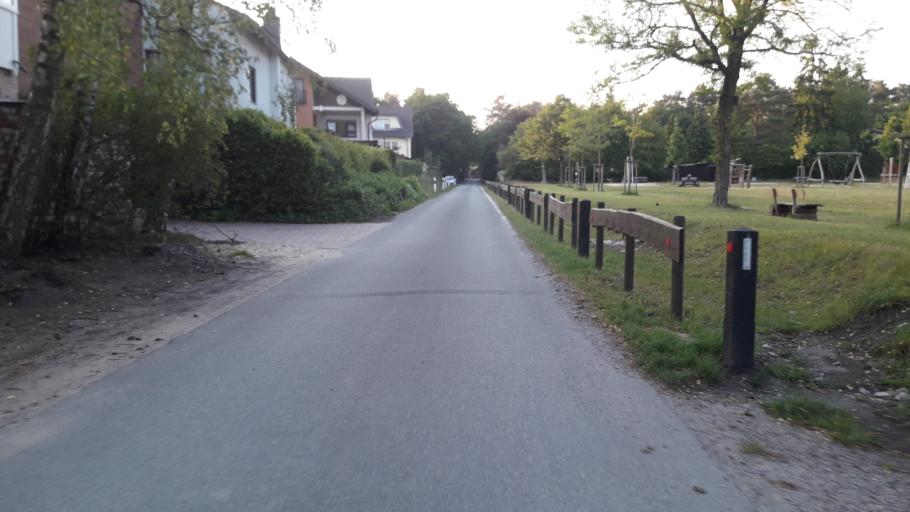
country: DE
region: North Rhine-Westphalia
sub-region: Regierungsbezirk Detmold
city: Augustdorf
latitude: 51.8687
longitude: 8.6921
